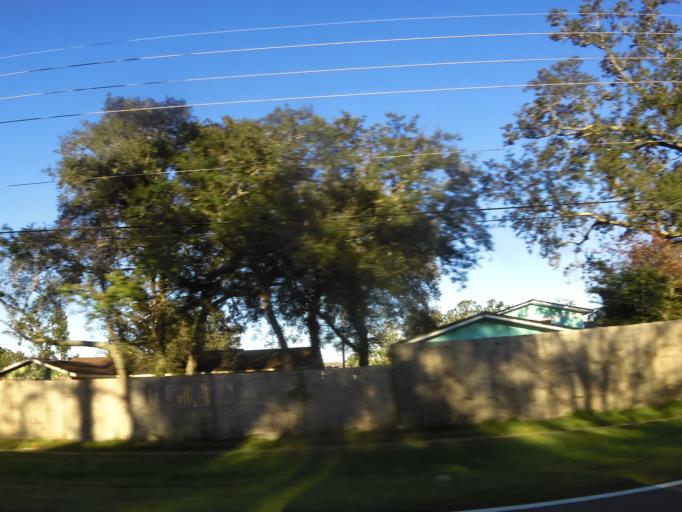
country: US
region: Florida
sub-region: Duval County
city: Neptune Beach
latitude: 30.3048
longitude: -81.4445
